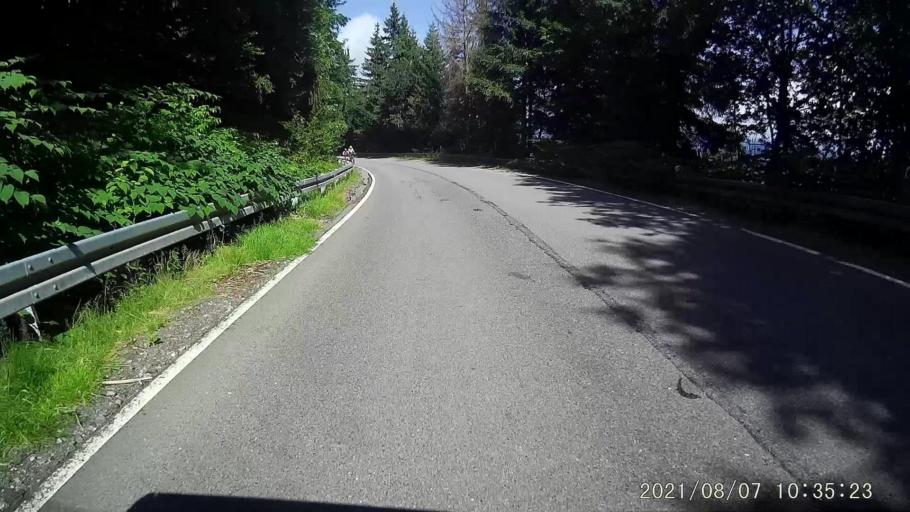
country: PL
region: Lower Silesian Voivodeship
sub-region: Powiat klodzki
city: Duszniki-Zdroj
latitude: 50.3690
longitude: 16.3709
